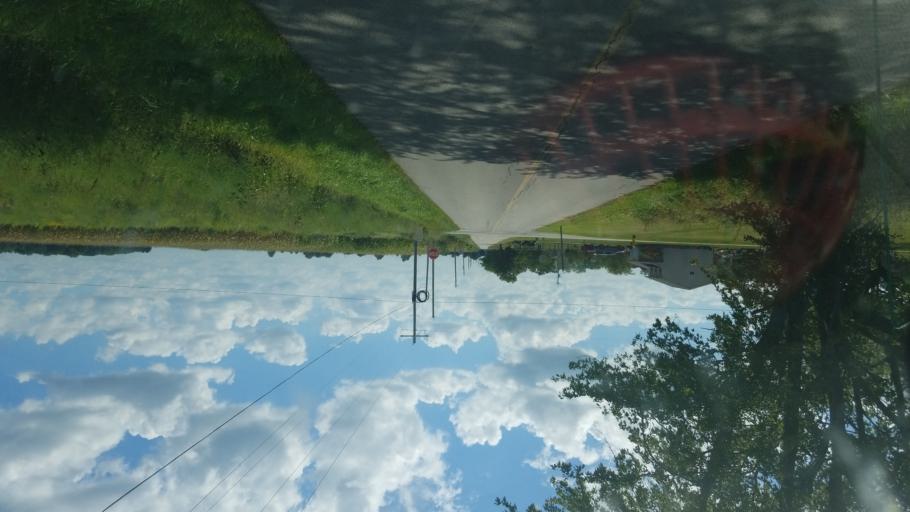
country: US
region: Ohio
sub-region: Union County
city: Richwood
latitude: 40.3167
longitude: -83.2365
